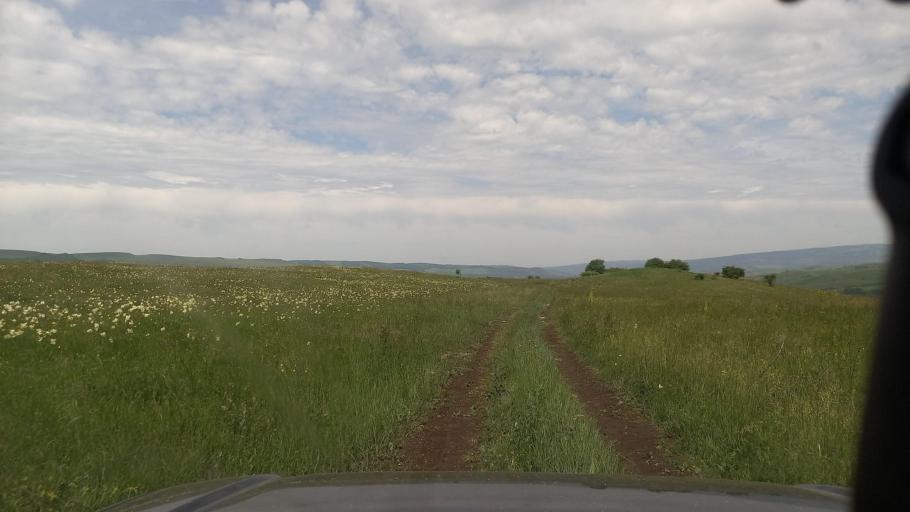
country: RU
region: Krasnodarskiy
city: Peredovaya
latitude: 44.0731
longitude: 41.3215
